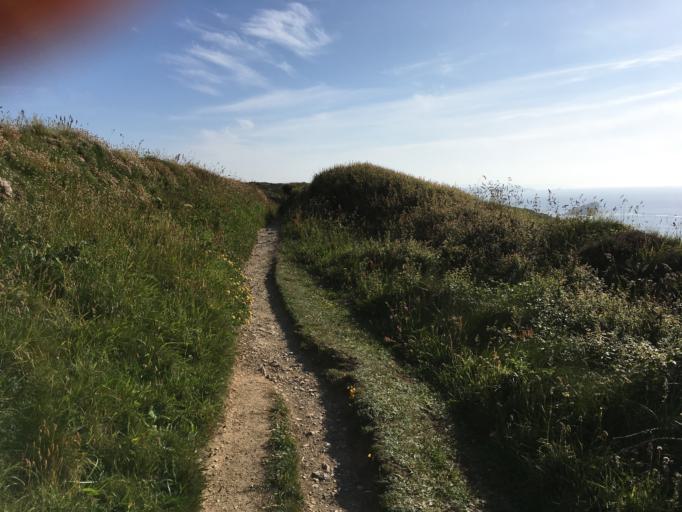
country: GB
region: England
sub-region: Cornwall
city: Camborne
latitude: 50.2682
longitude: -5.2839
